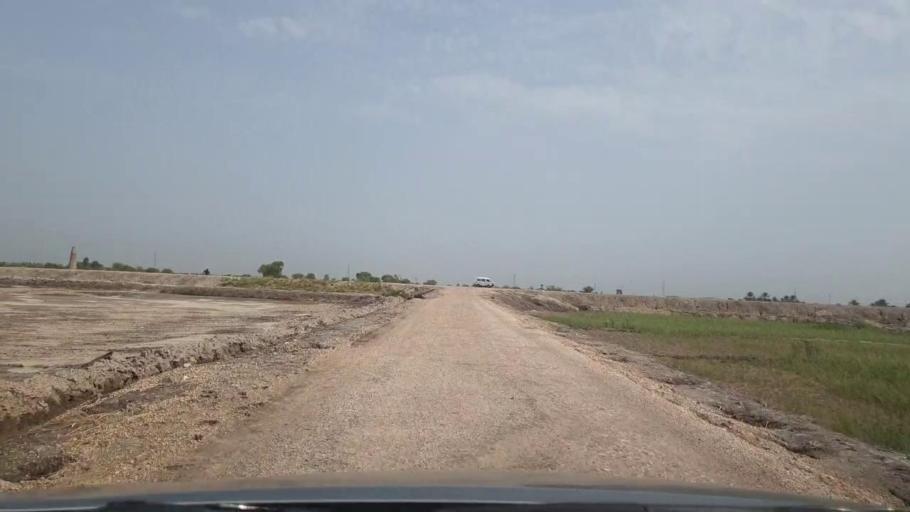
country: PK
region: Sindh
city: Rohri
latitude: 27.6782
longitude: 69.0257
